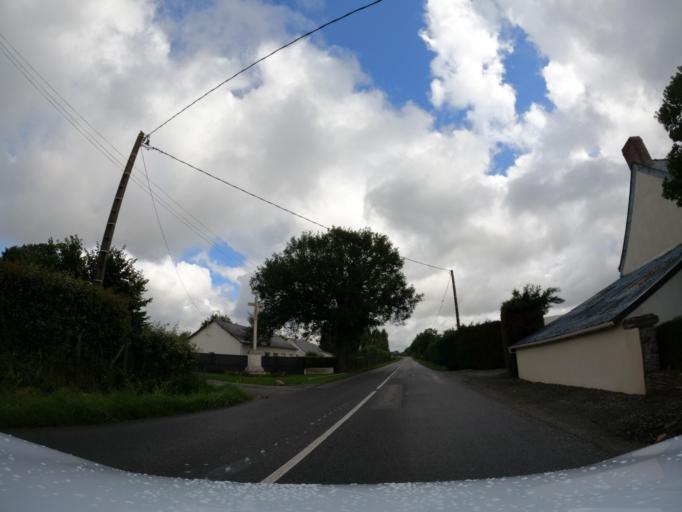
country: FR
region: Pays de la Loire
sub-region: Departement de la Loire-Atlantique
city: Ligne
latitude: 47.3924
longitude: -1.3834
